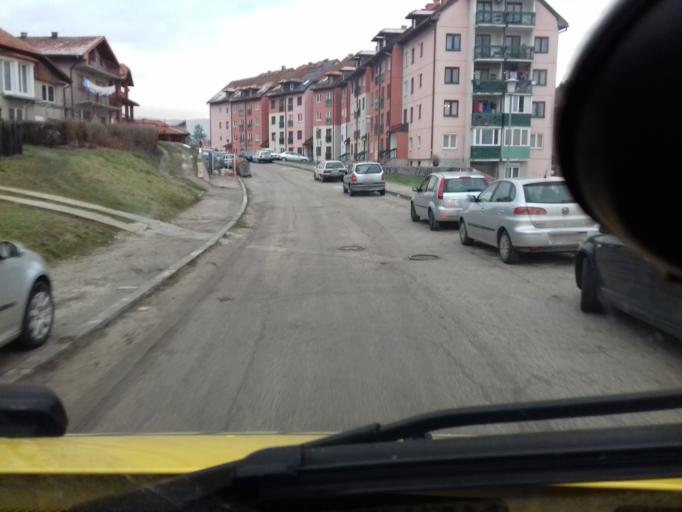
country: BA
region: Federation of Bosnia and Herzegovina
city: Zenica
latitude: 44.1941
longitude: 17.9424
